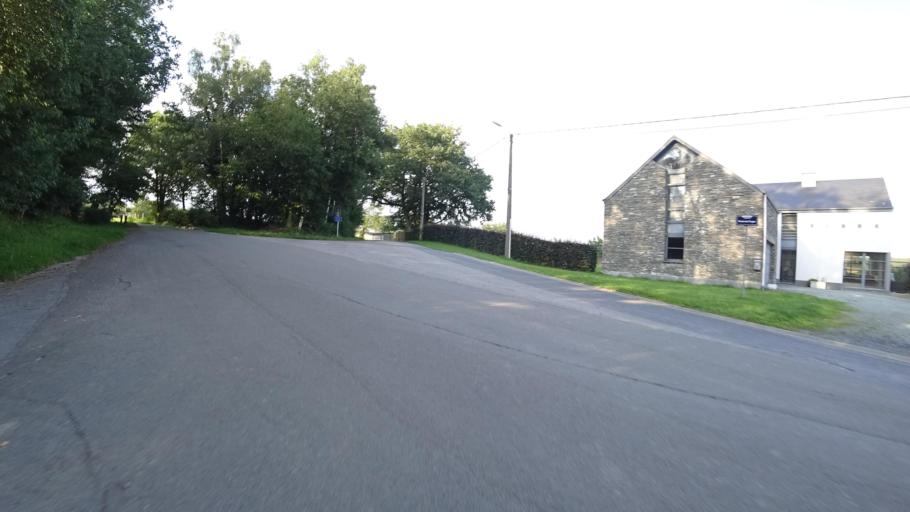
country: BE
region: Wallonia
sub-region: Province du Luxembourg
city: Neufchateau
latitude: 49.8654
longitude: 5.3722
